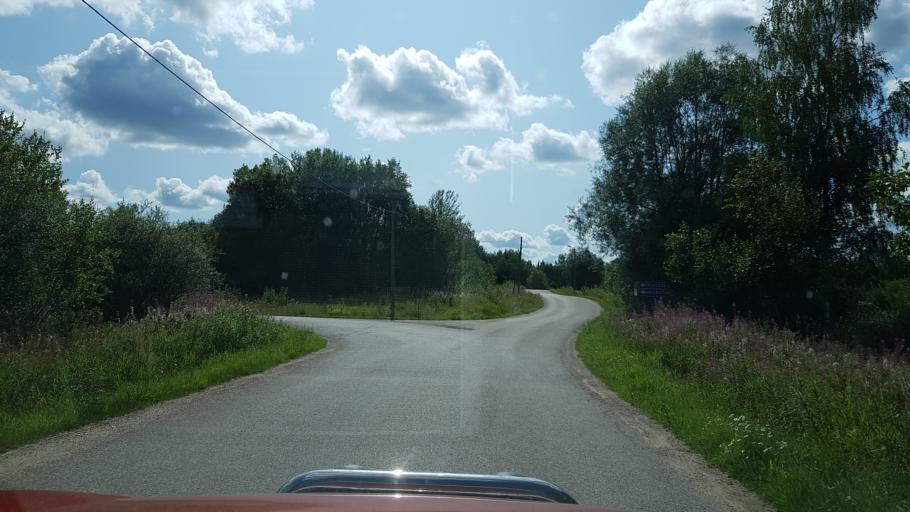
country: EE
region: Vorumaa
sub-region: Voru linn
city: Voru
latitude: 57.6327
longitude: 27.0901
